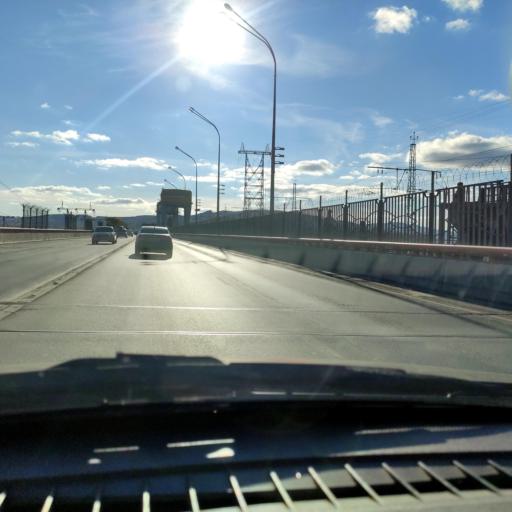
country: RU
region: Samara
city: Zhigulevsk
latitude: 53.4559
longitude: 49.4952
